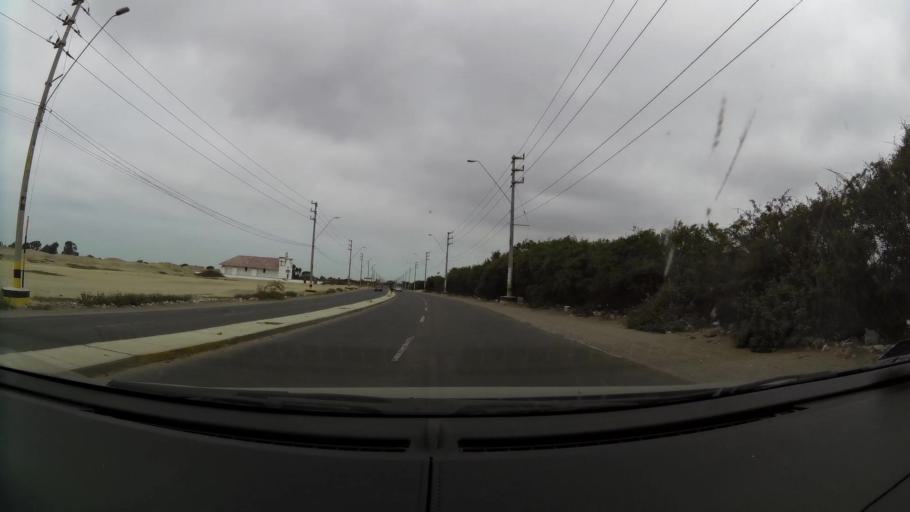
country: PE
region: La Libertad
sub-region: Provincia de Trujillo
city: La Esperanza
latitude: -8.0938
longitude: -79.0733
